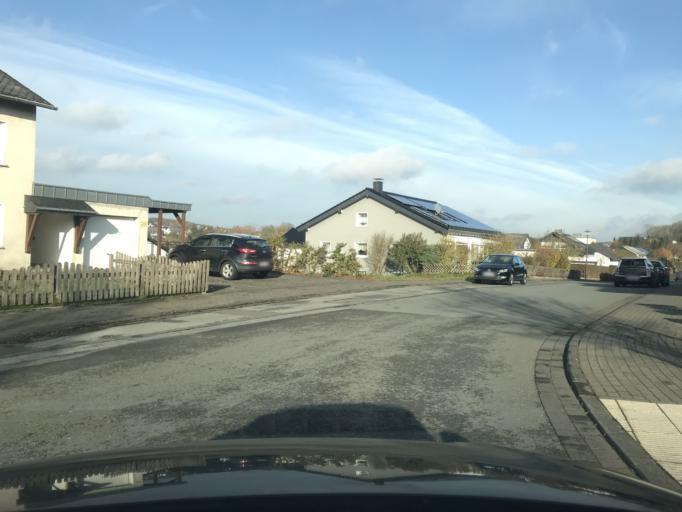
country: DE
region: North Rhine-Westphalia
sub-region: Regierungsbezirk Arnsberg
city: Brilon
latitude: 51.3898
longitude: 8.5550
